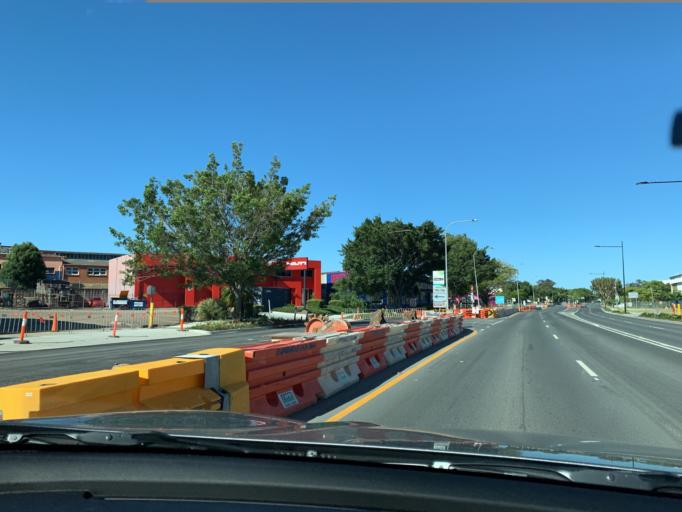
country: AU
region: Queensland
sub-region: Brisbane
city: Ascot
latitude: -27.4354
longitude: 153.0763
